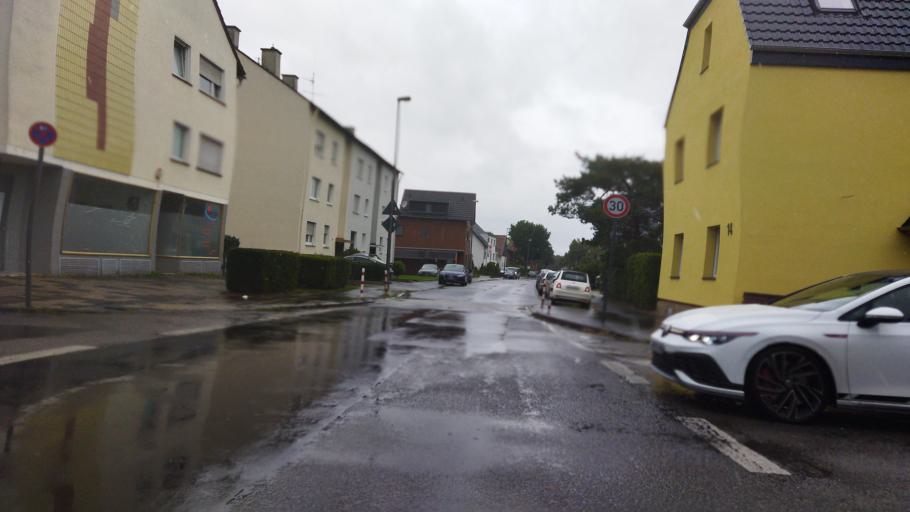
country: DE
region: North Rhine-Westphalia
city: Wesseling
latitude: 50.8487
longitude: 6.9735
